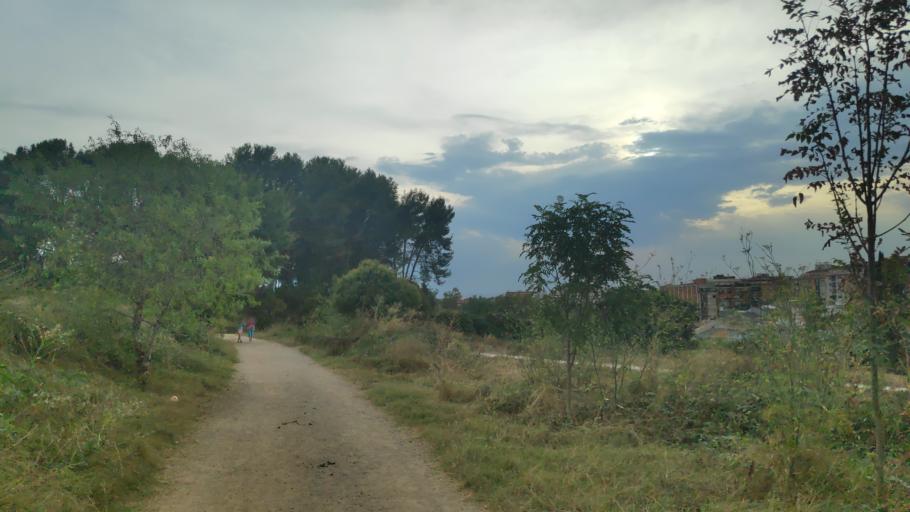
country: ES
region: Catalonia
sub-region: Provincia de Barcelona
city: Rubi
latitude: 41.4955
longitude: 2.0443
